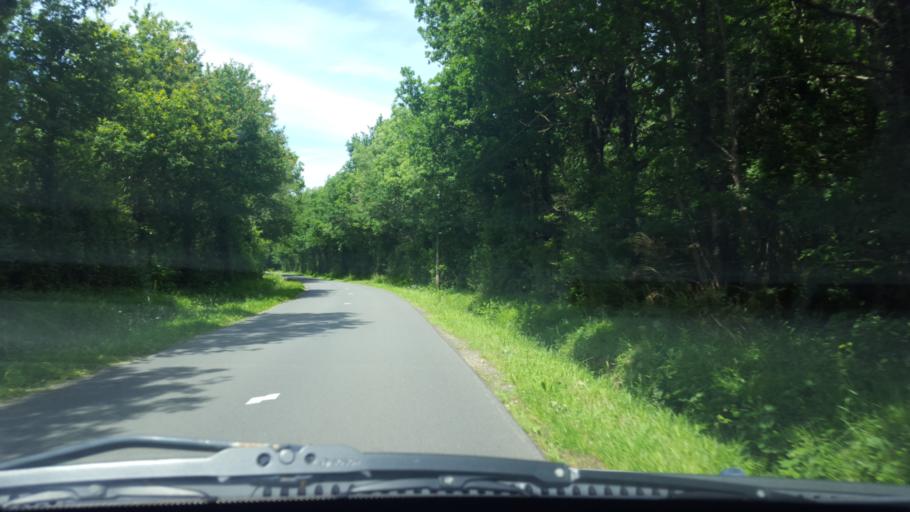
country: FR
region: Pays de la Loire
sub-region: Departement de la Loire-Atlantique
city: La Limouziniere
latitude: 47.0177
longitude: -1.5833
